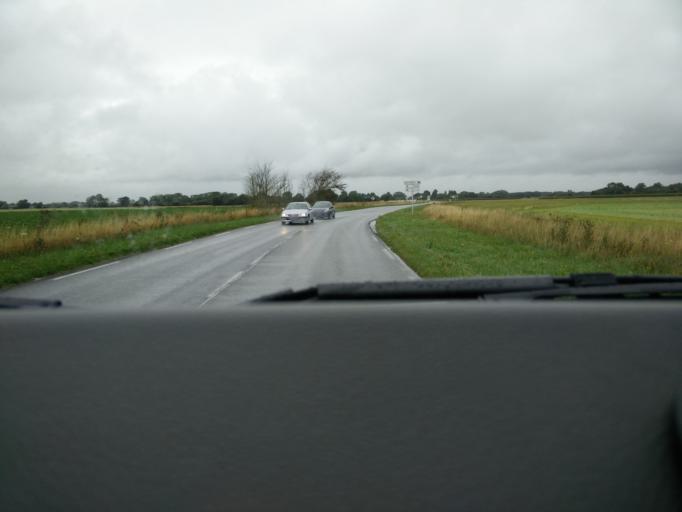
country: FR
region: Picardie
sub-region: Departement de la Somme
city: Le Crotoy
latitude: 50.2364
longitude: 1.6449
